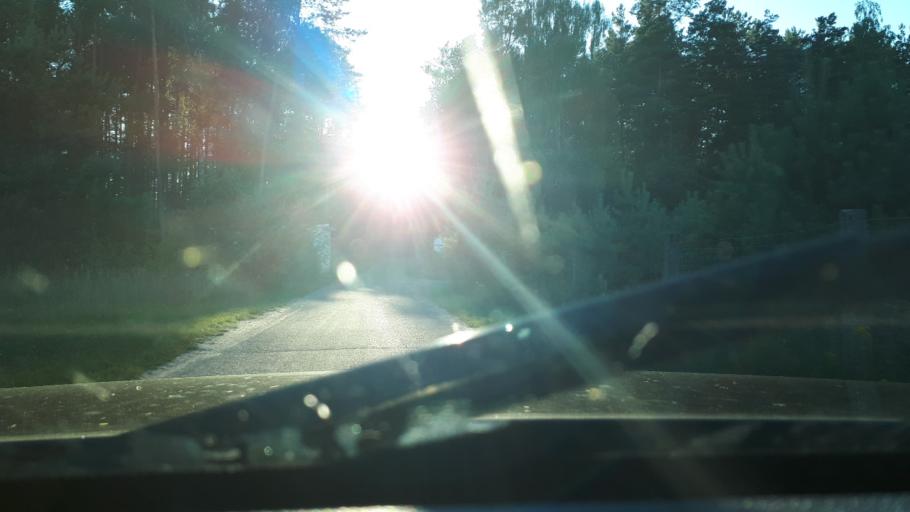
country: PL
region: Warmian-Masurian Voivodeship
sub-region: Powiat olsztynski
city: Stawiguda
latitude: 53.5872
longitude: 20.4618
